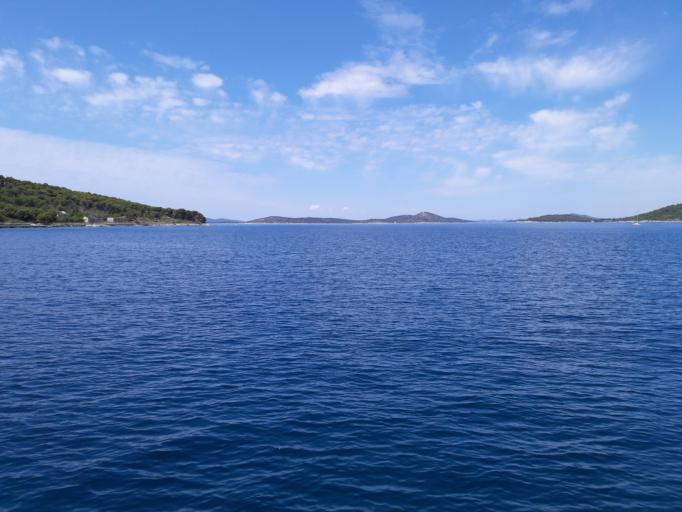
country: HR
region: Sibensko-Kniniska
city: Vodice
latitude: 43.7012
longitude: 15.8311
